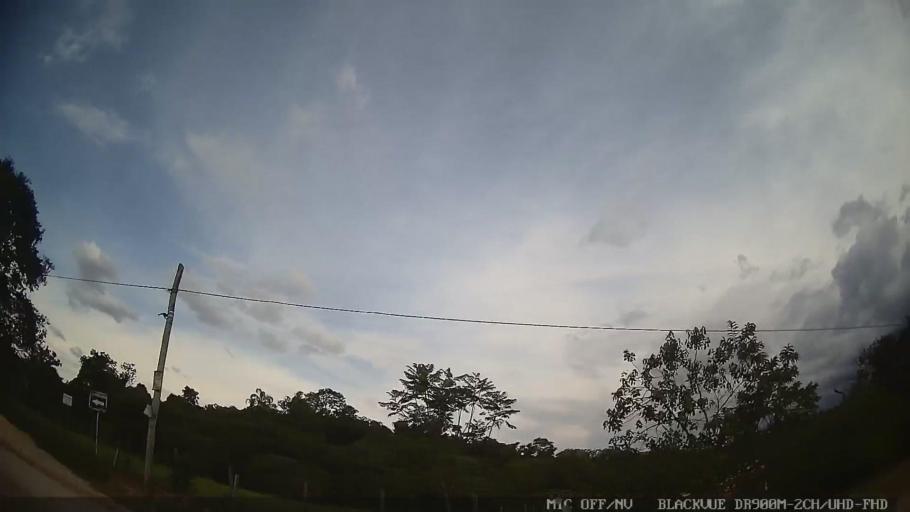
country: BR
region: Sao Paulo
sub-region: Amparo
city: Amparo
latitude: -22.7736
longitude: -46.7644
